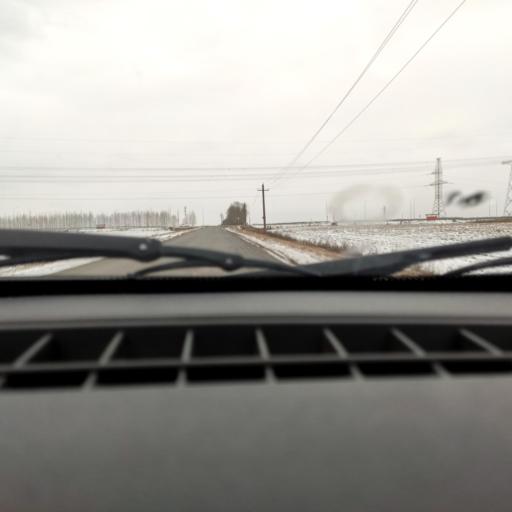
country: RU
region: Bashkortostan
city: Tolbazy
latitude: 54.2479
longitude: 55.8858
